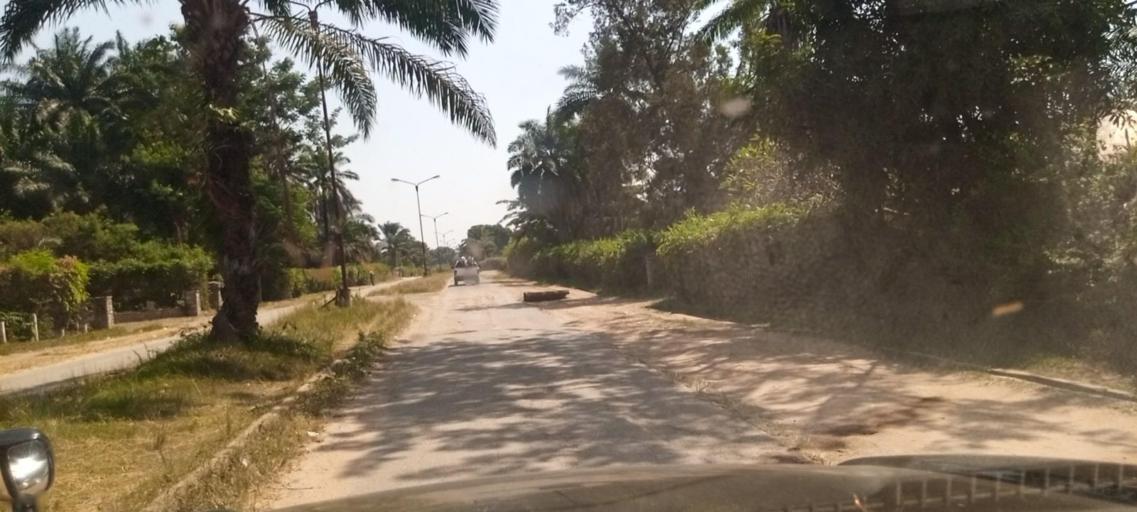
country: CD
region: Kasai-Oriental
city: Mbuji-Mayi
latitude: -6.1231
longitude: 23.5907
